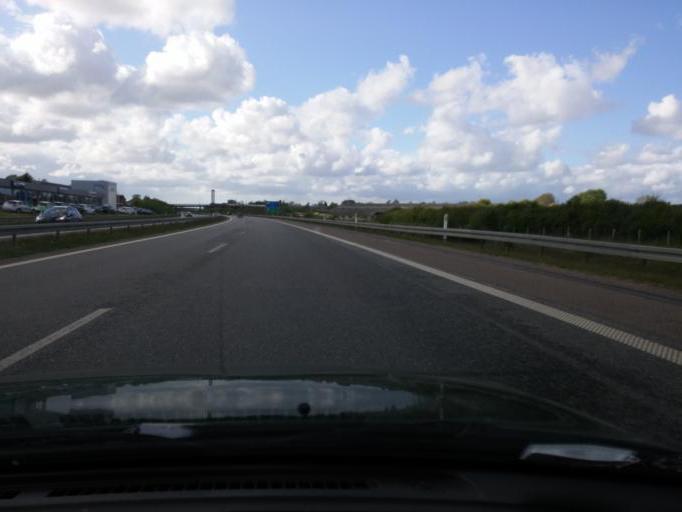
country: DK
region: South Denmark
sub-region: Faaborg-Midtfyn Kommune
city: Ringe
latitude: 55.2416
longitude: 10.4884
